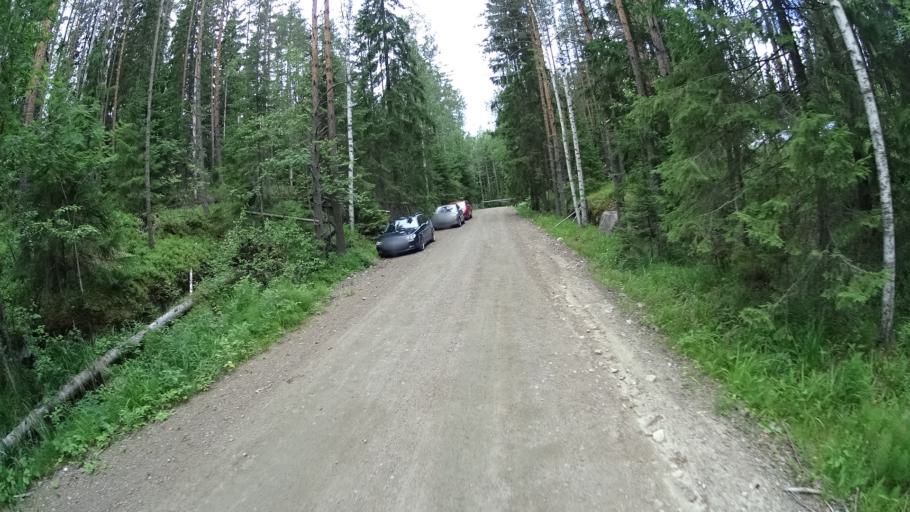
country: FI
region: Southern Savonia
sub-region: Mikkeli
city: Maentyharju
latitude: 61.1554
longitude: 26.8861
